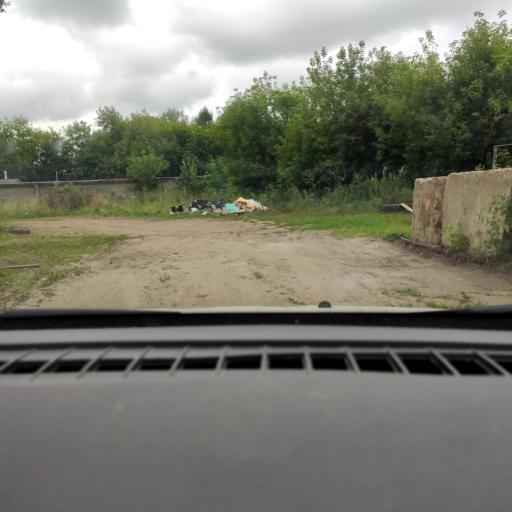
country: RU
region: Perm
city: Polazna
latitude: 58.1222
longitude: 56.3849
